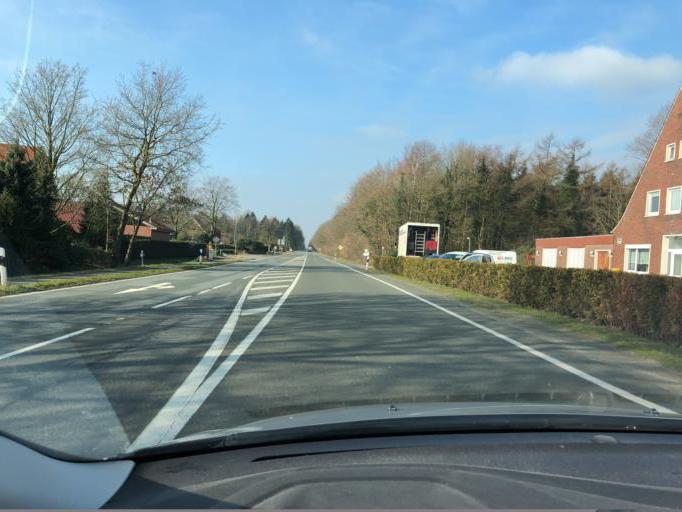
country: DE
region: Lower Saxony
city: Firrel
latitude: 53.3072
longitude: 7.6513
